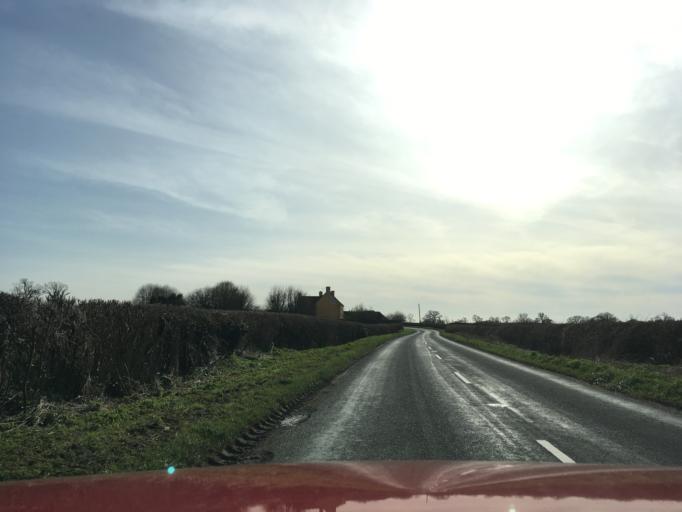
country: GB
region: England
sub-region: Wiltshire
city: Luckington
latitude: 51.5402
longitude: -2.2552
